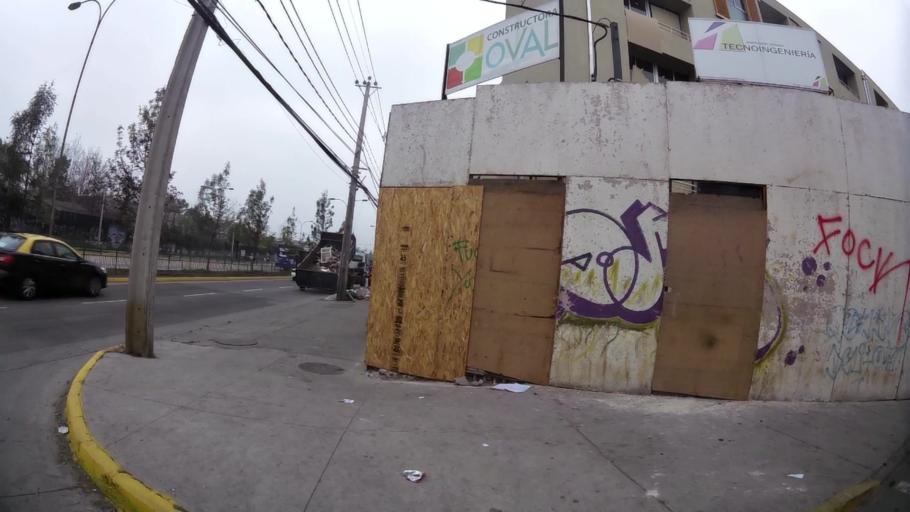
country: CL
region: Santiago Metropolitan
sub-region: Provincia de Santiago
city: Santiago
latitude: -33.4852
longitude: -70.6410
